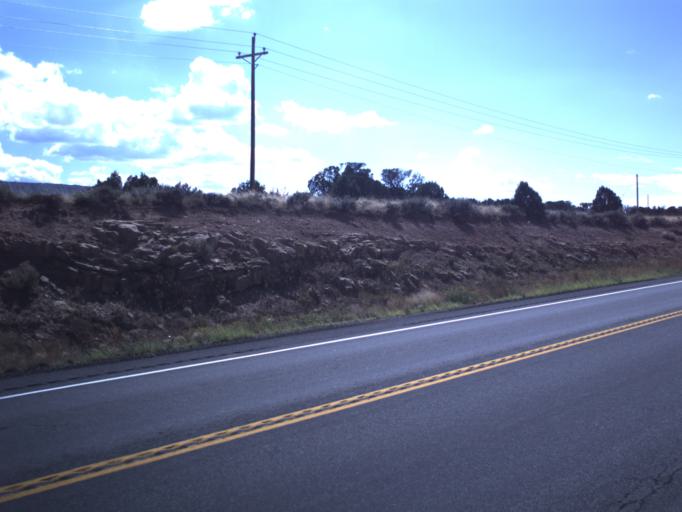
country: US
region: Utah
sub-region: Duchesne County
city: Duchesne
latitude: 40.2059
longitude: -110.8069
